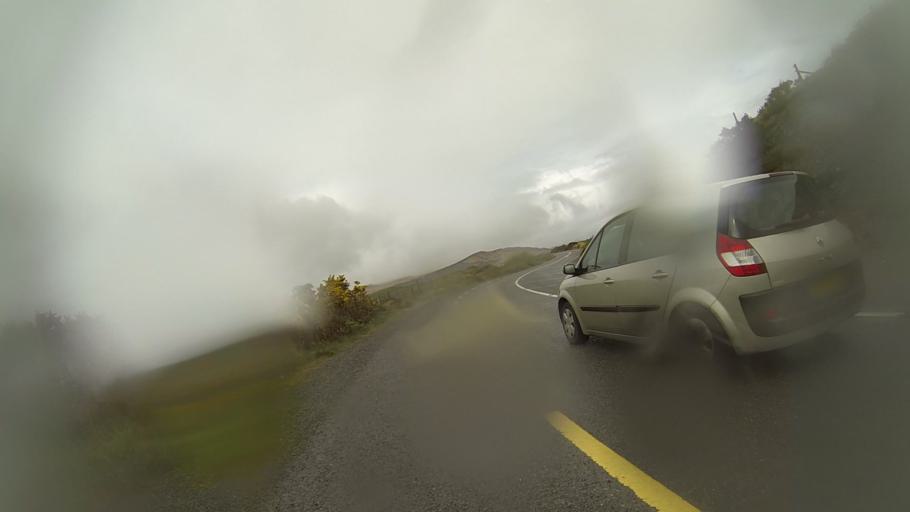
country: IE
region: Munster
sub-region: Ciarrai
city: Kenmare
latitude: 51.8004
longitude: -9.5704
